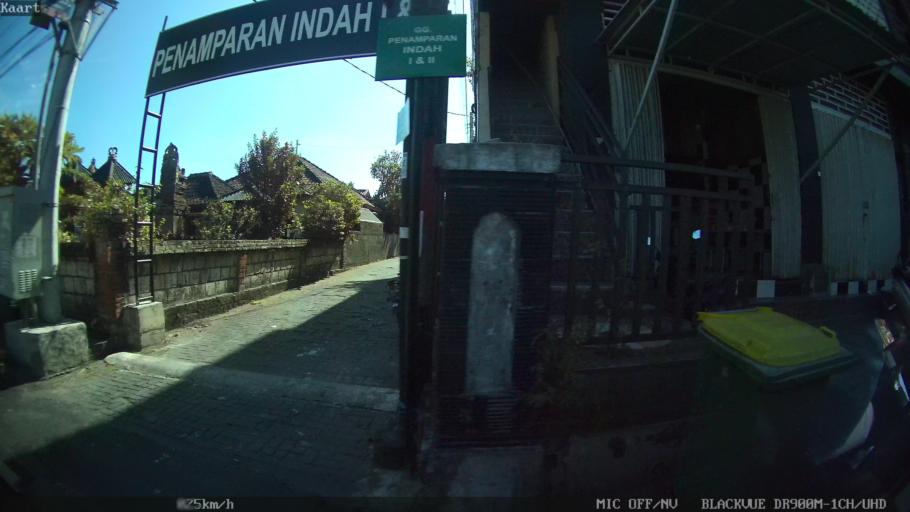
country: ID
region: Bali
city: Denpasar
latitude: -8.6430
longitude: 115.1911
